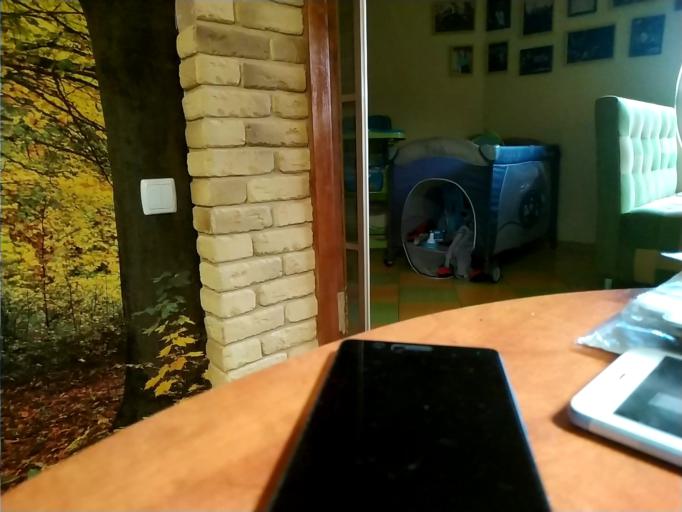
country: RU
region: Kaluga
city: Khvastovichi
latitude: 53.6279
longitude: 35.4588
